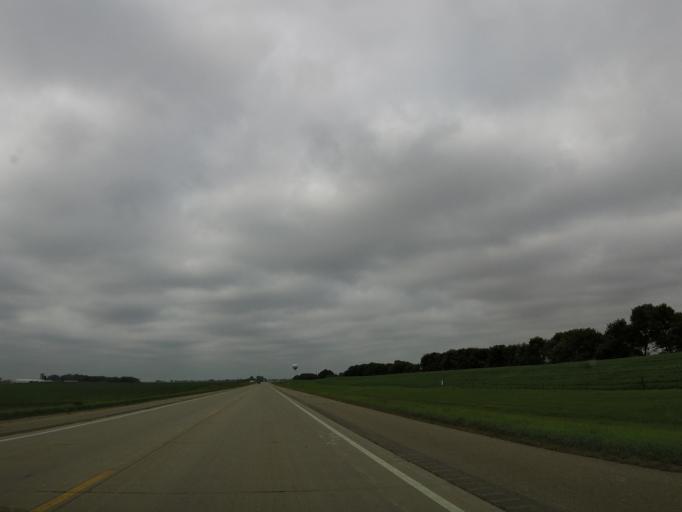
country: US
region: Minnesota
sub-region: Renville County
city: Renville
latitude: 44.7893
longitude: -95.1644
